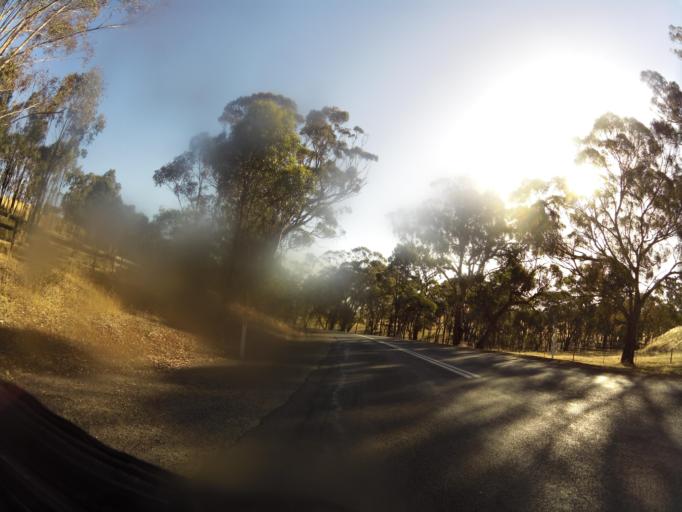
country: AU
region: Victoria
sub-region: Murrindindi
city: Kinglake West
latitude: -37.0120
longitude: 145.1192
